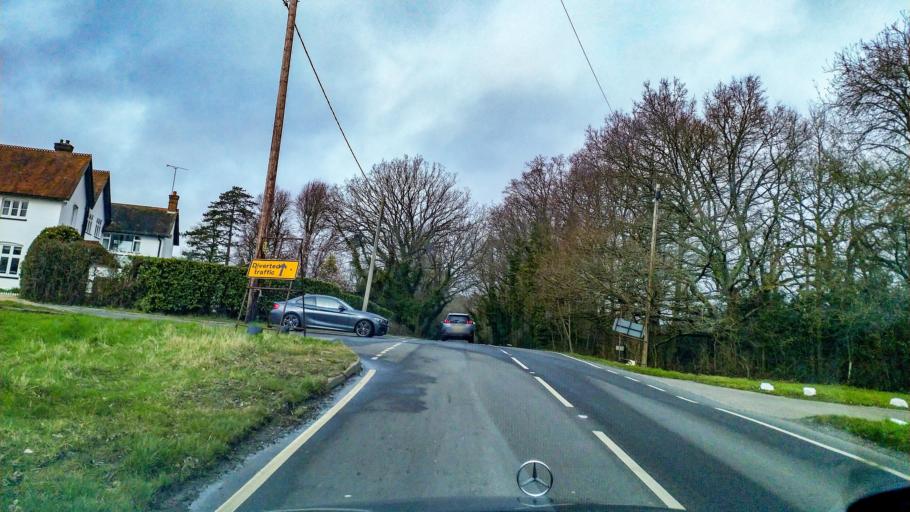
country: GB
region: England
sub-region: Surrey
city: Dorking
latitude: 51.2147
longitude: -0.3135
